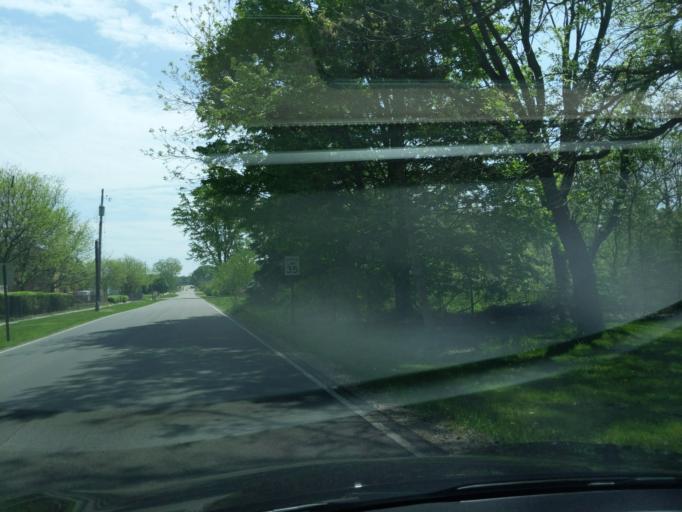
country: US
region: Michigan
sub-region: Ingham County
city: Holt
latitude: 42.6475
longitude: -84.5137
